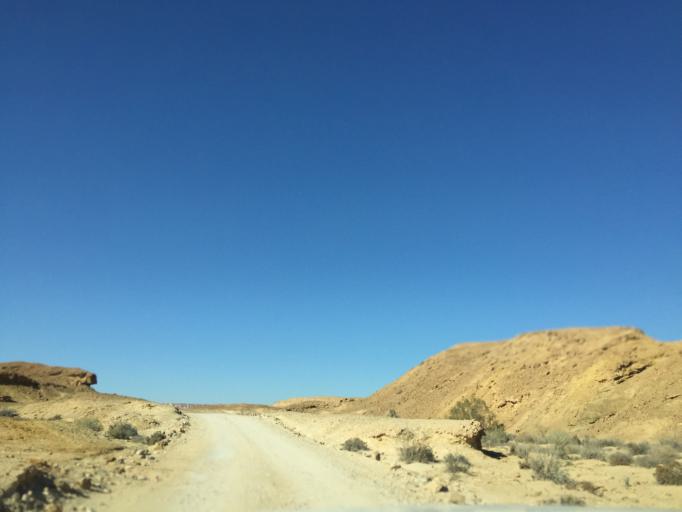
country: IL
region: Southern District
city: Mitzpe Ramon
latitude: 30.6076
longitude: 34.9379
